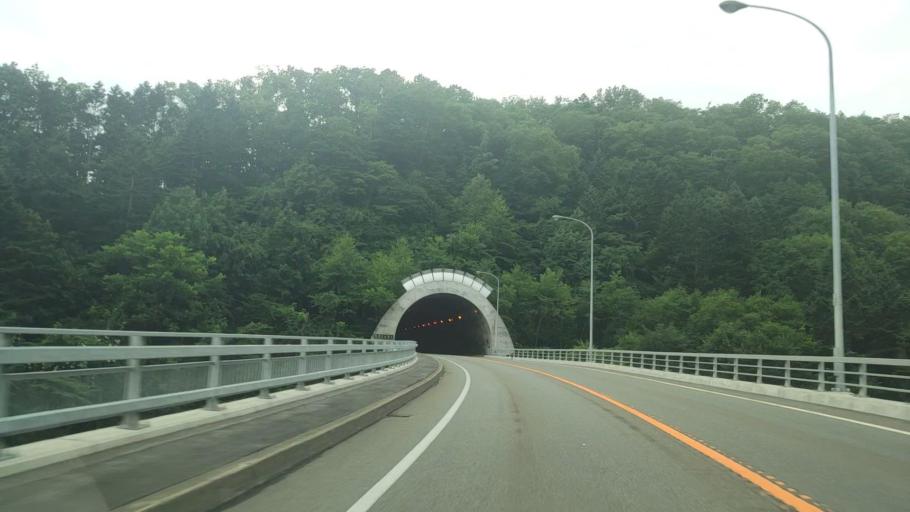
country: JP
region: Hokkaido
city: Niseko Town
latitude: 42.6041
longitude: 140.5604
